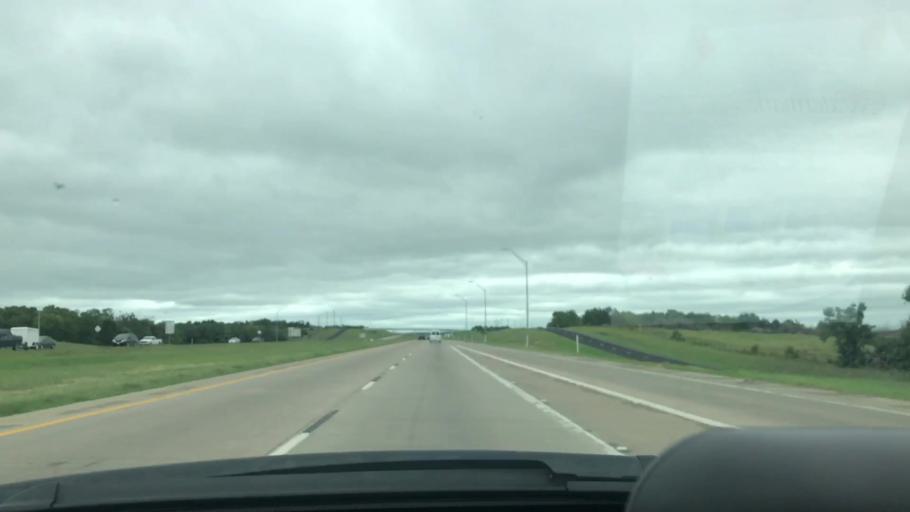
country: US
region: Texas
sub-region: Grayson County
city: Sherman
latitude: 33.6858
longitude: -96.6046
